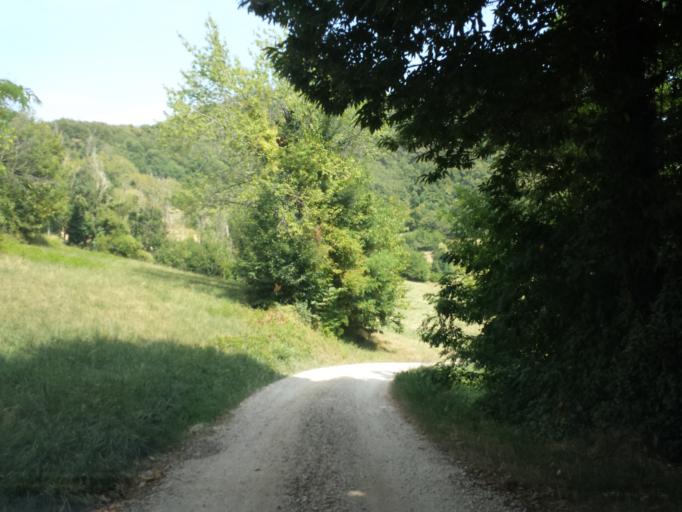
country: IT
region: Veneto
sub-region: Provincia di Vicenza
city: Cornedo Vicentino
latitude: 45.6384
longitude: 11.3311
